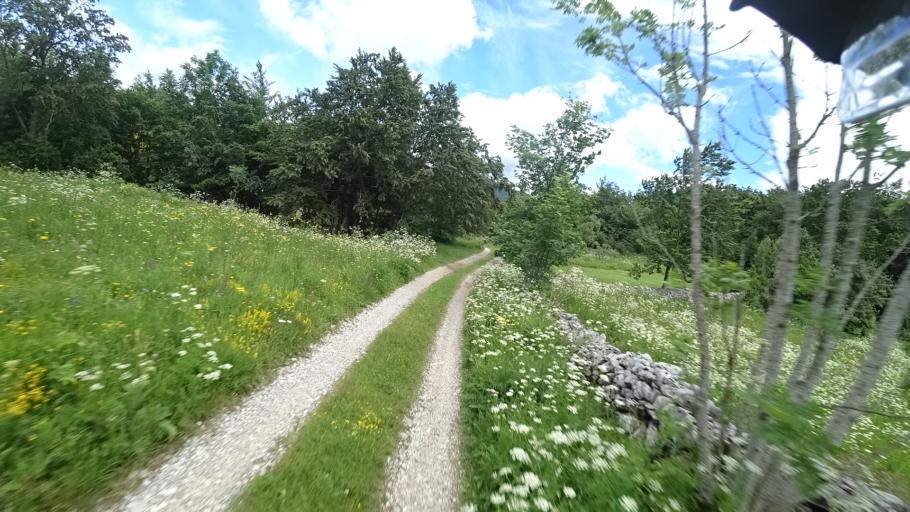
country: HR
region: Primorsko-Goranska
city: Bribir
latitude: 45.2370
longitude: 14.7720
